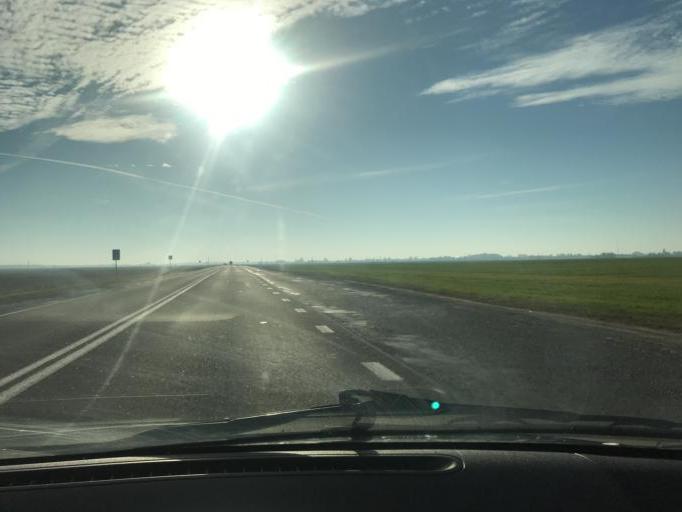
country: BY
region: Brest
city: Drahichyn
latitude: 52.2034
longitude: 25.2288
